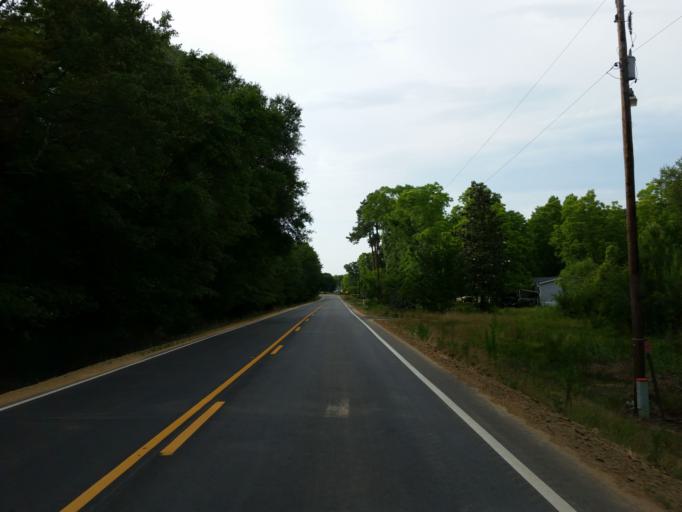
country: US
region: Georgia
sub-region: Turner County
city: Ashburn
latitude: 31.7627
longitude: -83.6846
